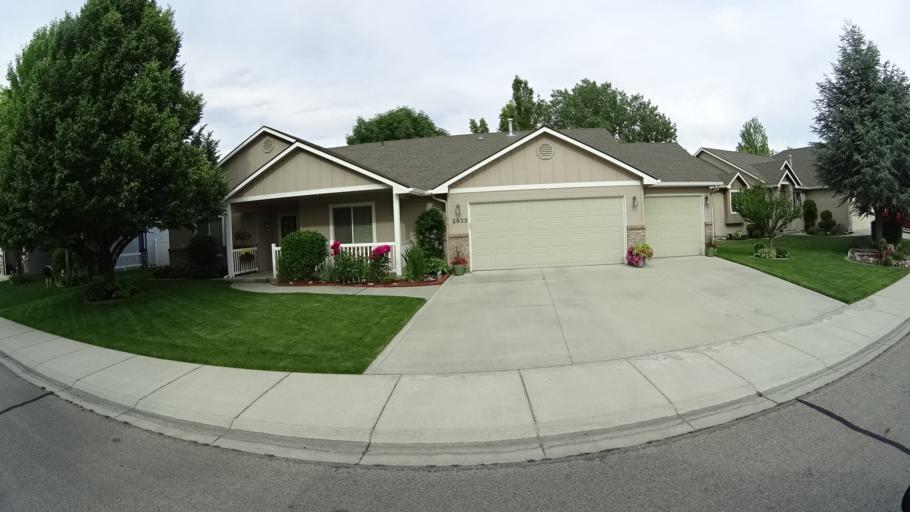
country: US
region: Idaho
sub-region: Ada County
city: Meridian
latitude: 43.5863
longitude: -116.3982
